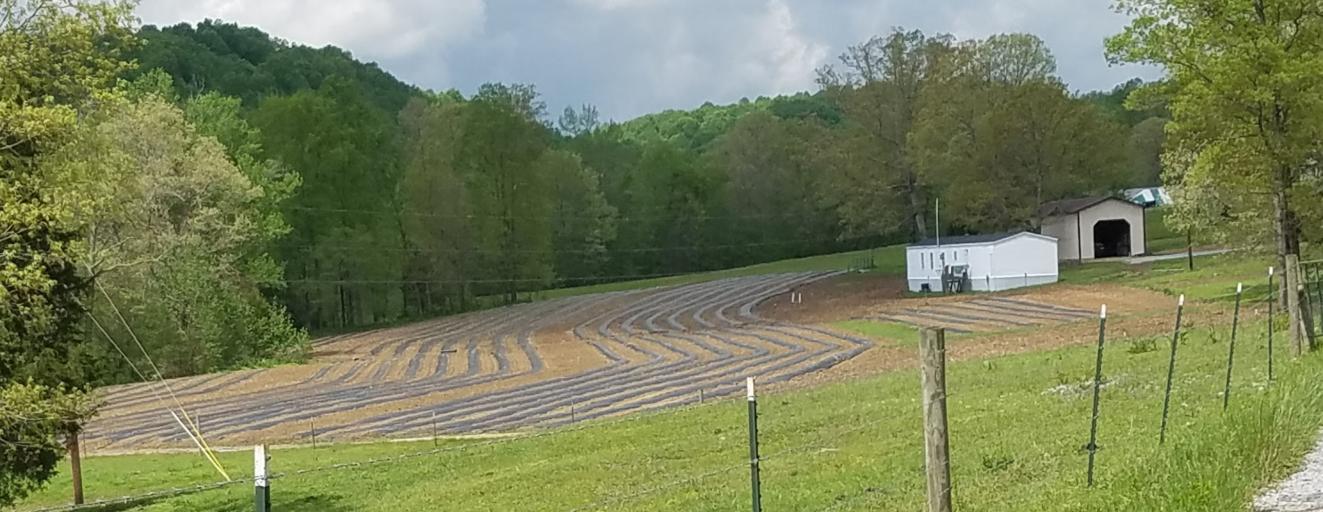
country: US
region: Kentucky
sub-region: Taylor County
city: Campbellsville
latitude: 37.4013
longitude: -85.2742
